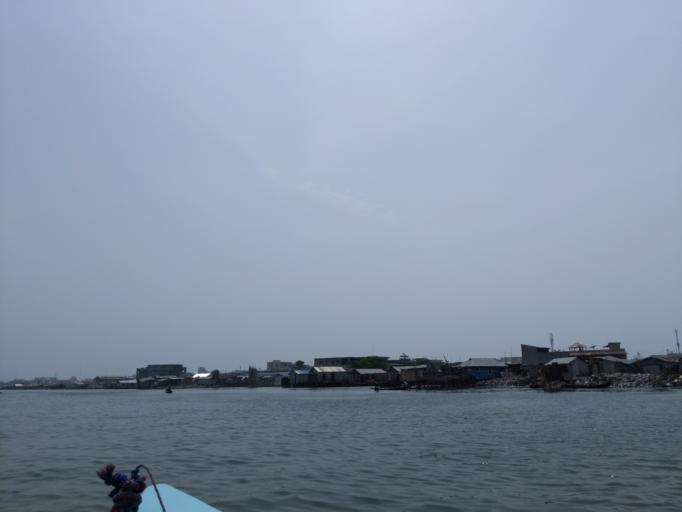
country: BJ
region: Littoral
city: Cotonou
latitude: 6.3836
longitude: 2.4349
